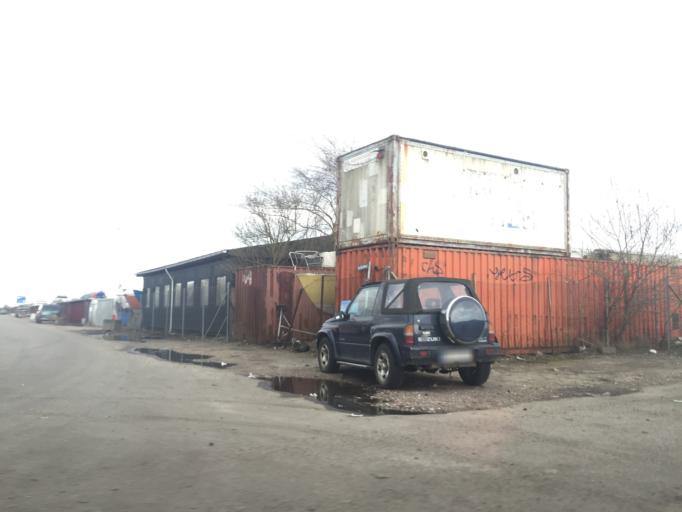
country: DK
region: Capital Region
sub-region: Frederiksberg Kommune
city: Frederiksberg
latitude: 55.6376
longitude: 12.5413
